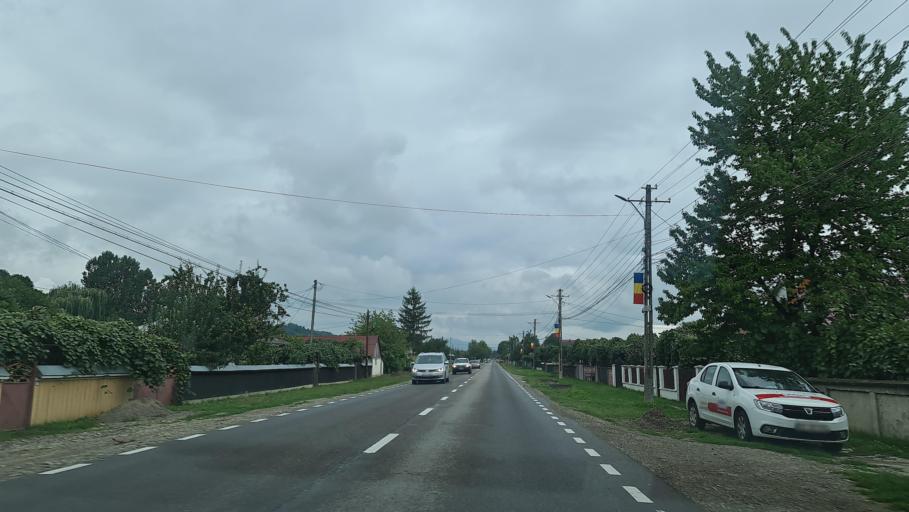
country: RO
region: Neamt
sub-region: Comuna Borlesti
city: Ruseni
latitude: 46.8063
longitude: 26.5247
